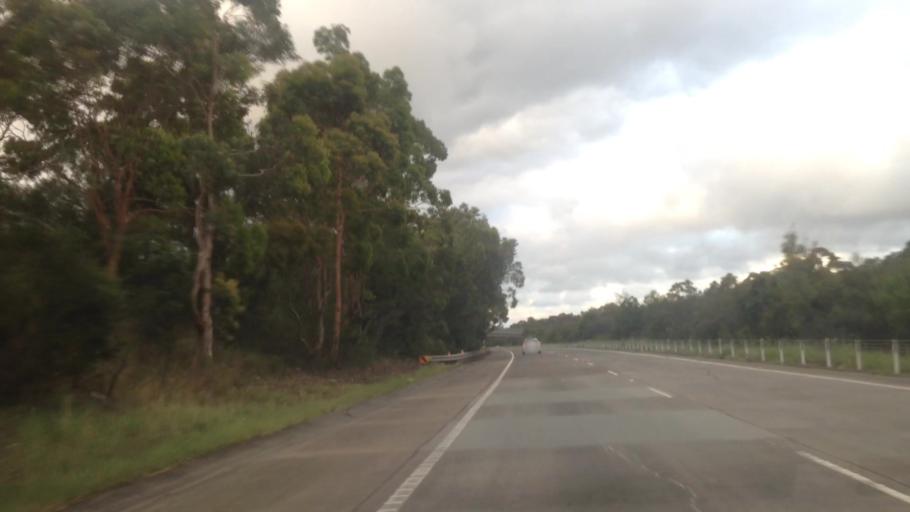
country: AU
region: New South Wales
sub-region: Wyong Shire
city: Charmhaven
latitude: -33.1980
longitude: 151.4637
